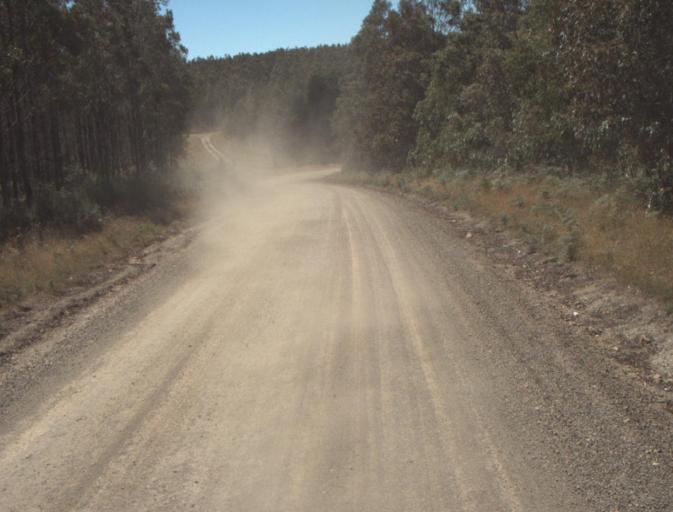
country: AU
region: Tasmania
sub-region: Dorset
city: Scottsdale
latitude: -41.3236
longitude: 147.4456
